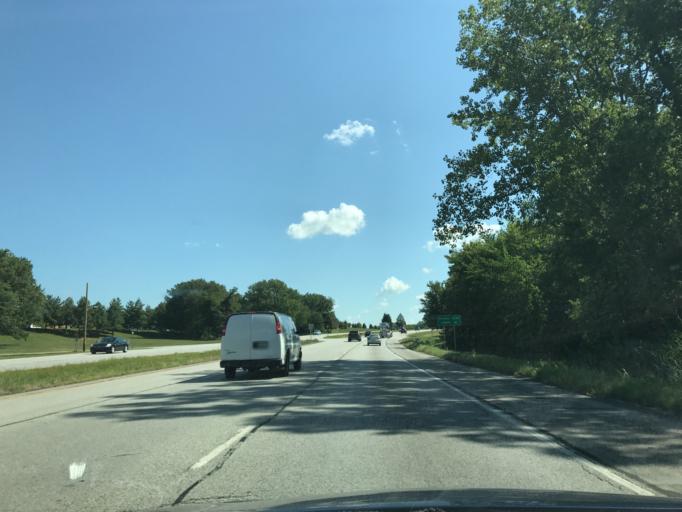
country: US
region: Indiana
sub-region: Porter County
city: Valparaiso
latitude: 41.4594
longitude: -87.0454
